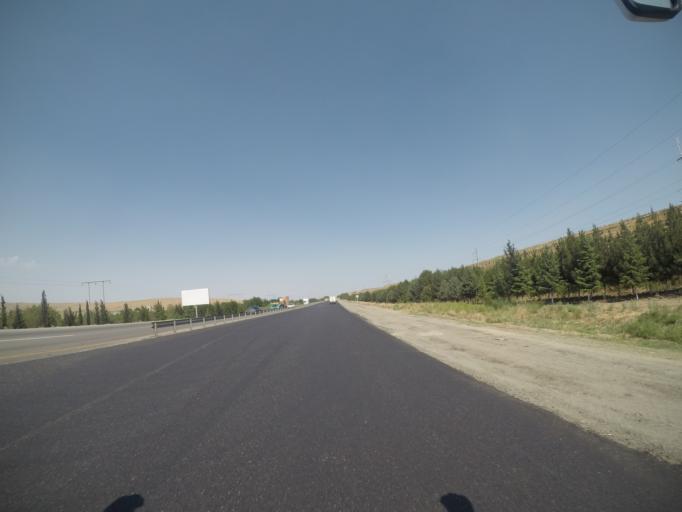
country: AZ
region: Haciqabul
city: Haciqabul
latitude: 40.0420
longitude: 48.9618
